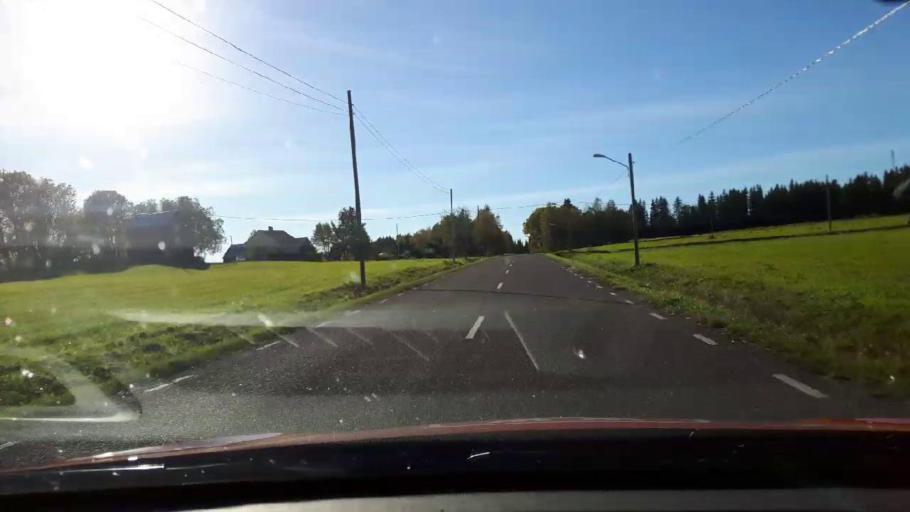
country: SE
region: Jaemtland
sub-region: Stroemsunds Kommun
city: Stroemsund
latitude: 63.8439
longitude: 15.3300
